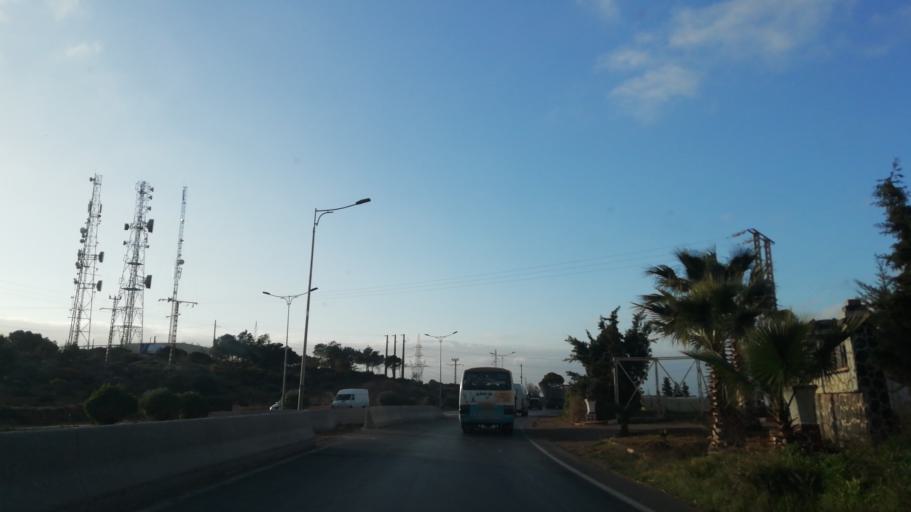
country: DZ
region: Oran
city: Oran
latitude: 35.6420
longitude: -0.7100
